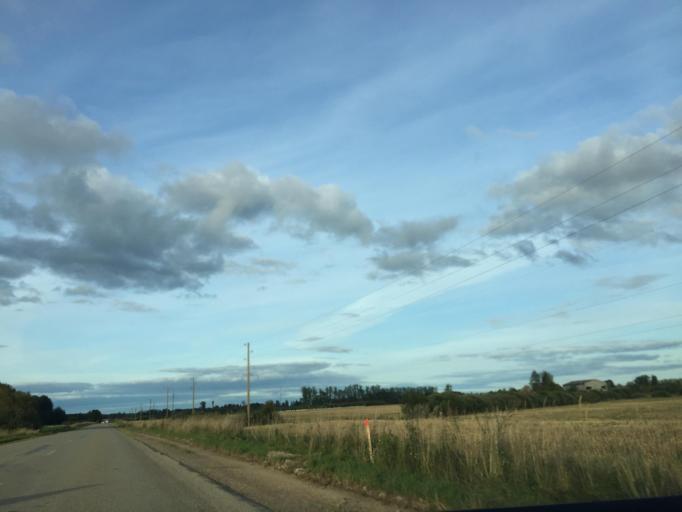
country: LV
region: Nereta
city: Nereta
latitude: 56.2675
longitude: 25.3690
